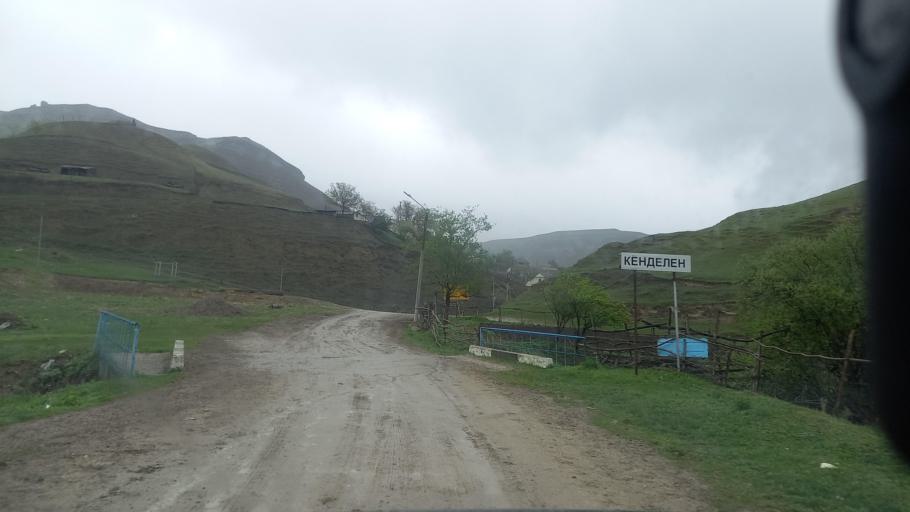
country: RU
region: Kabardino-Balkariya
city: Gundelen
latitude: 43.5990
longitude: 43.1450
